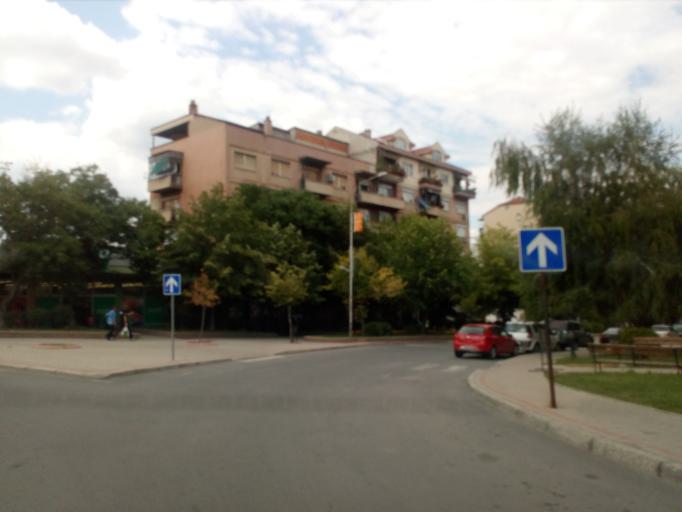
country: MK
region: Veles
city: Veles
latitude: 41.7152
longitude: 21.7694
